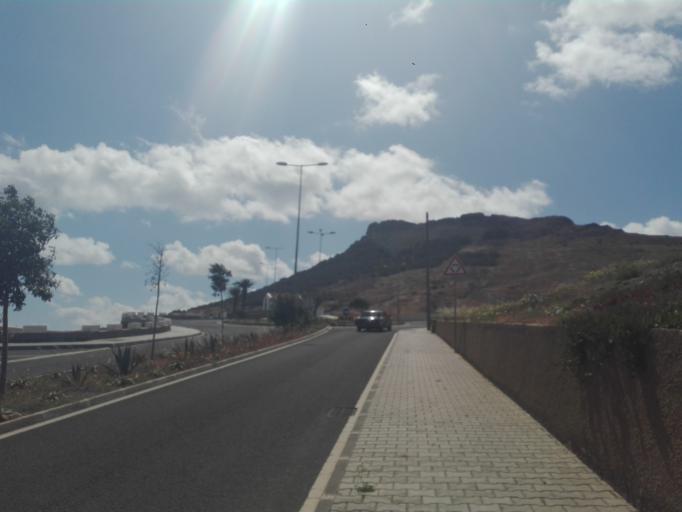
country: PT
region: Madeira
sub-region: Porto Santo
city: Vila de Porto Santo
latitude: 33.0464
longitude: -16.3608
